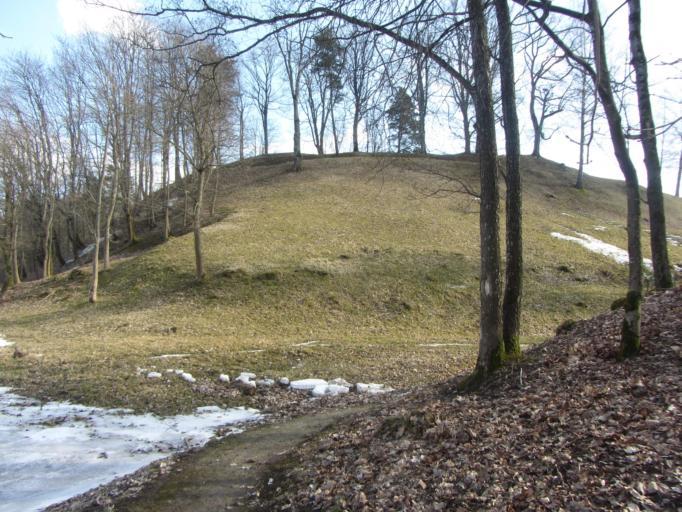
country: LT
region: Taurages apskritis
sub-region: Jurbarkas
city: Jurbarkas
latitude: 55.0484
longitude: 22.6453
